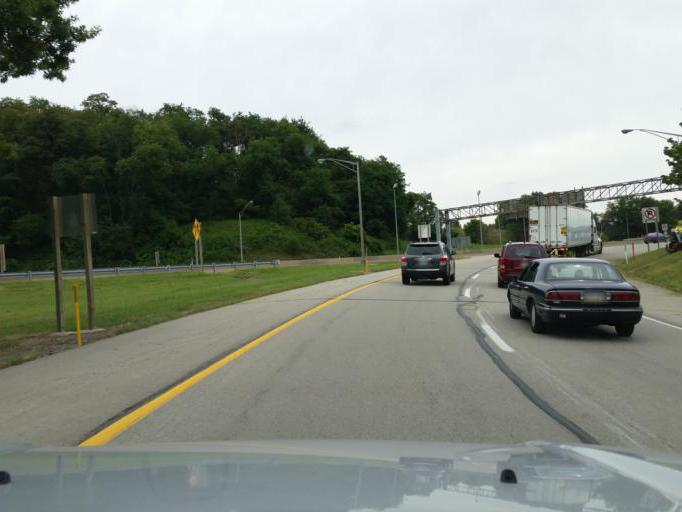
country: US
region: Pennsylvania
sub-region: Allegheny County
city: Monroeville
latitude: 40.4380
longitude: -79.7553
